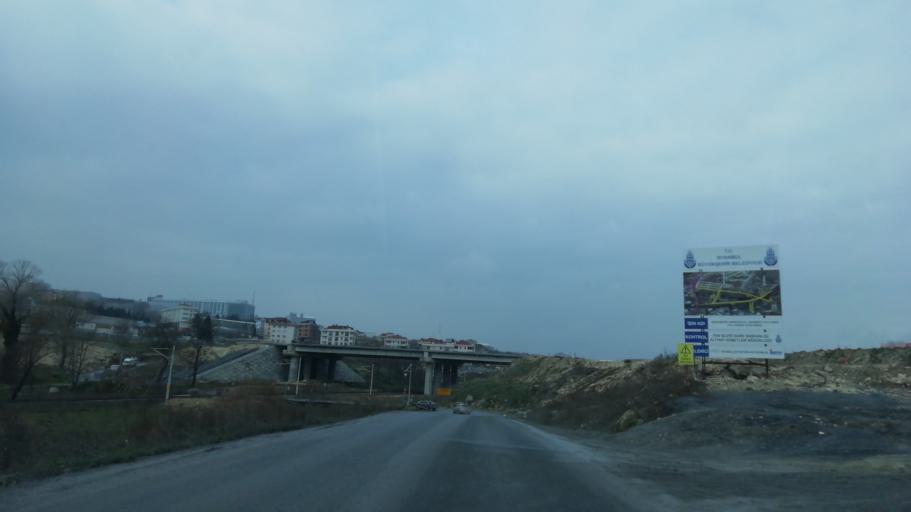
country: TR
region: Istanbul
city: Esenyurt
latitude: 41.1122
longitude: 28.6471
